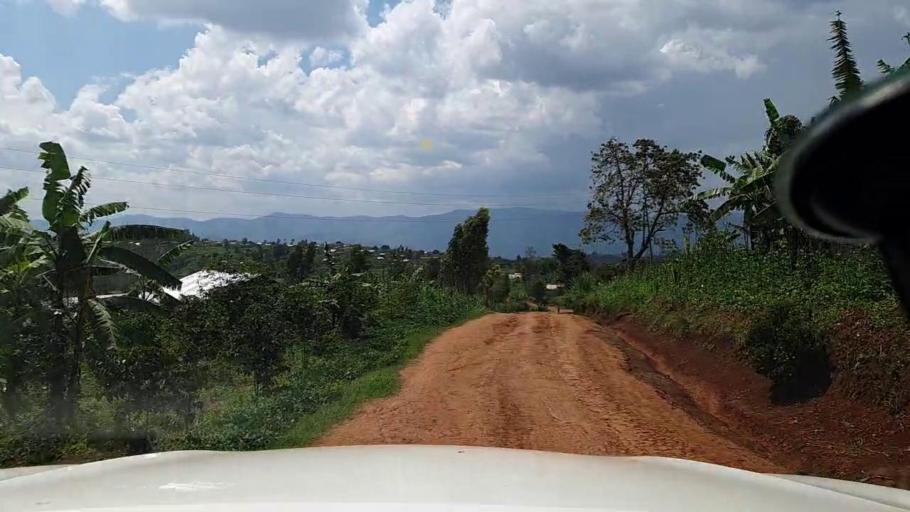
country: RW
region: Kigali
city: Kigali
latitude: -1.8332
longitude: 29.8423
